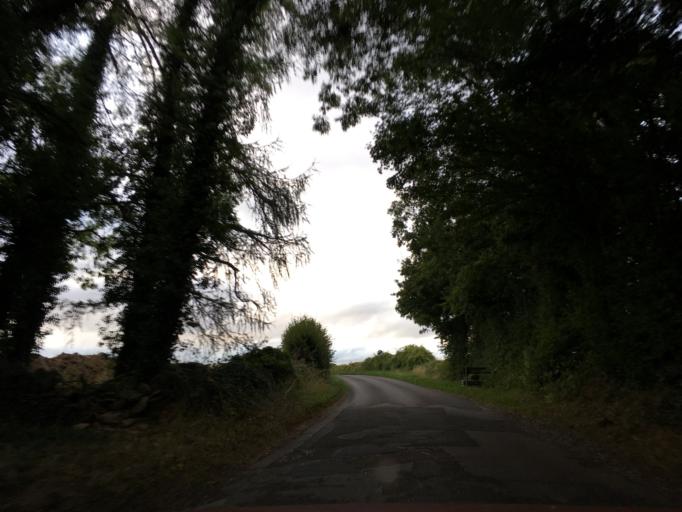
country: GB
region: England
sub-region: Wiltshire
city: Biddestone
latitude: 51.4645
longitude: -2.2005
